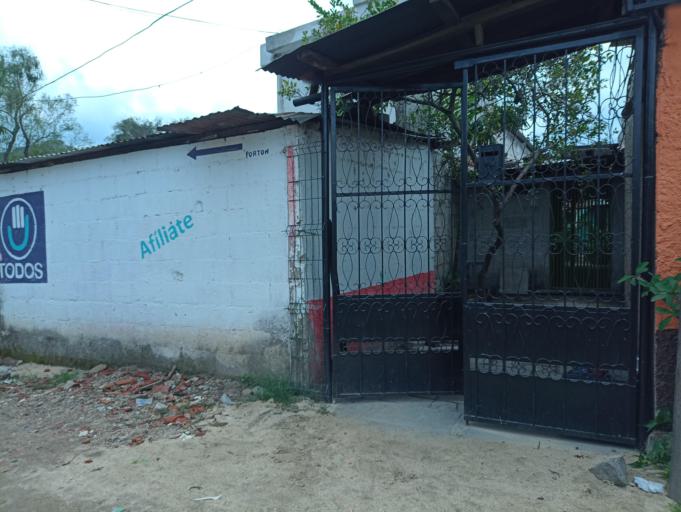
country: GT
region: Guatemala
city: Villa Canales
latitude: 14.4894
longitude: -90.5368
